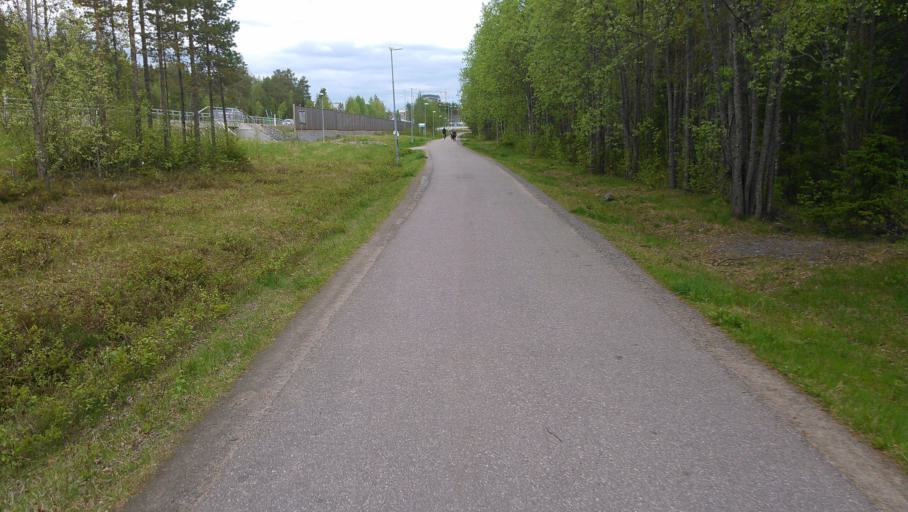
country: SE
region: Vaesterbotten
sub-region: Umea Kommun
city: Ersmark
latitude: 63.8264
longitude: 20.3317
